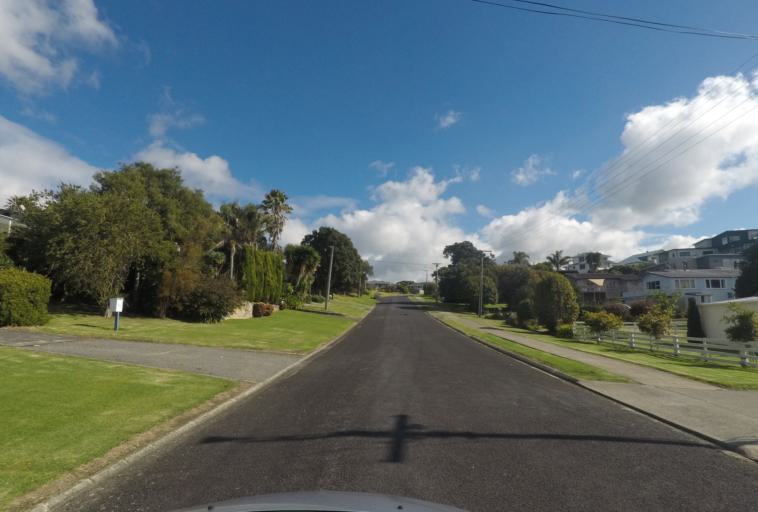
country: NZ
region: Bay of Plenty
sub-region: Western Bay of Plenty District
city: Waihi Beach
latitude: -37.4139
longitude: 175.9406
